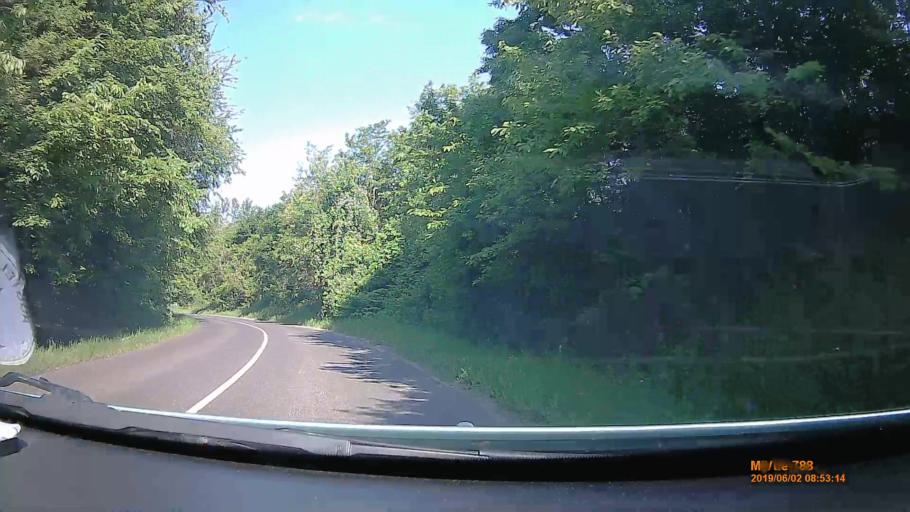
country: HU
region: Borsod-Abauj-Zemplen
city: Sajobabony
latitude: 48.1508
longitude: 20.6829
